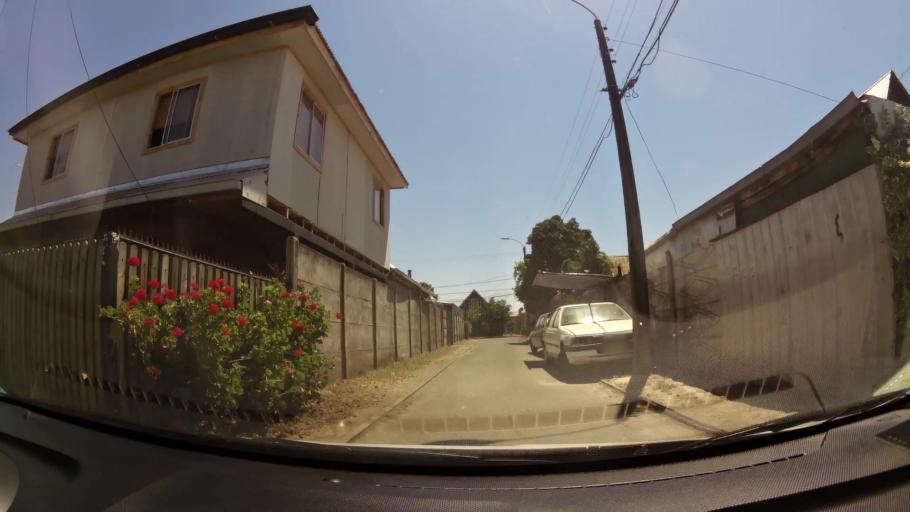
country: CL
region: Maule
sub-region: Provincia de Curico
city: Curico
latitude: -34.9801
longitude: -71.2176
